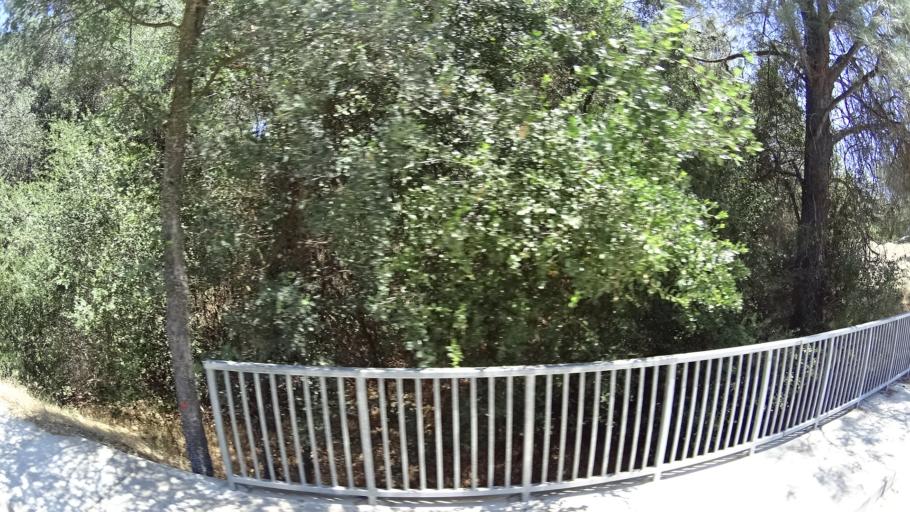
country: US
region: California
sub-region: Calaveras County
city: Rancho Calaveras
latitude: 38.1359
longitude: -120.8660
